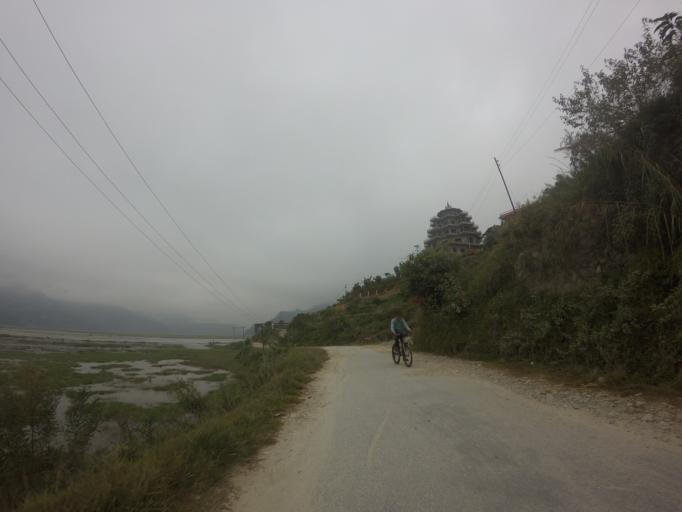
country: NP
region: Western Region
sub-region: Gandaki Zone
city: Pokhara
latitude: 28.2278
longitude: 83.9341
